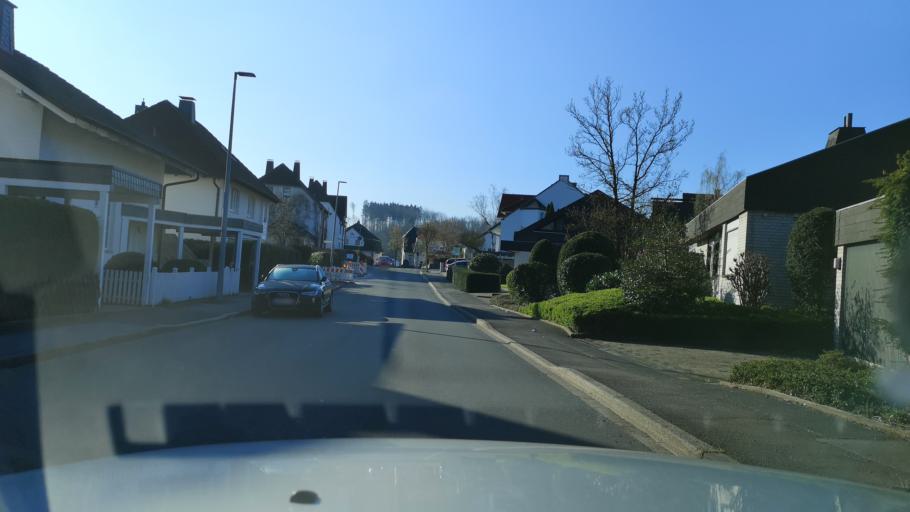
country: DE
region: North Rhine-Westphalia
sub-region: Regierungsbezirk Arnsberg
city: Menden
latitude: 51.4333
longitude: 7.7845
